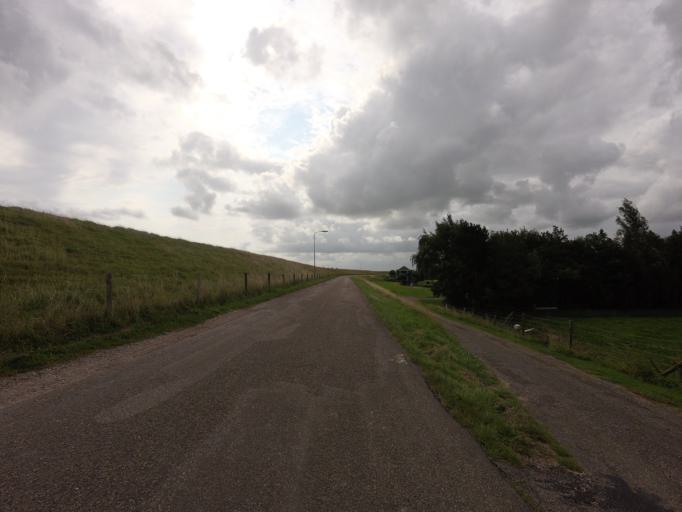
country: NL
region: North Holland
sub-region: Gemeente Hoorn
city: Hoorn
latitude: 52.6138
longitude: 5.0189
